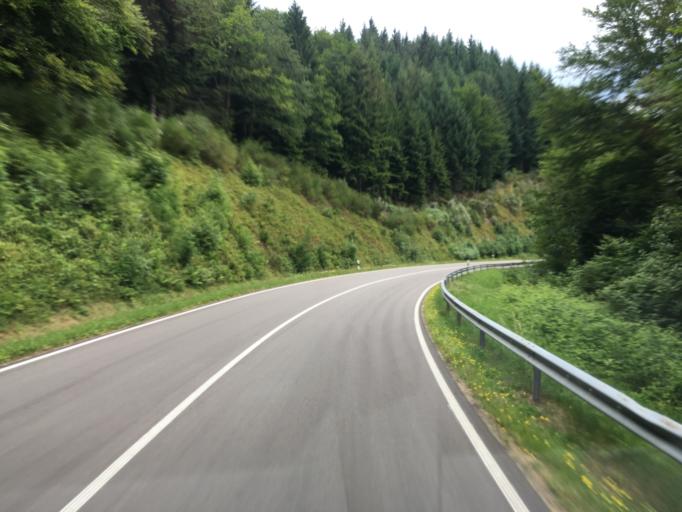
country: DE
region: Baden-Wuerttemberg
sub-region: Karlsruhe Region
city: Buhlertal
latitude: 48.7085
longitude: 8.2319
